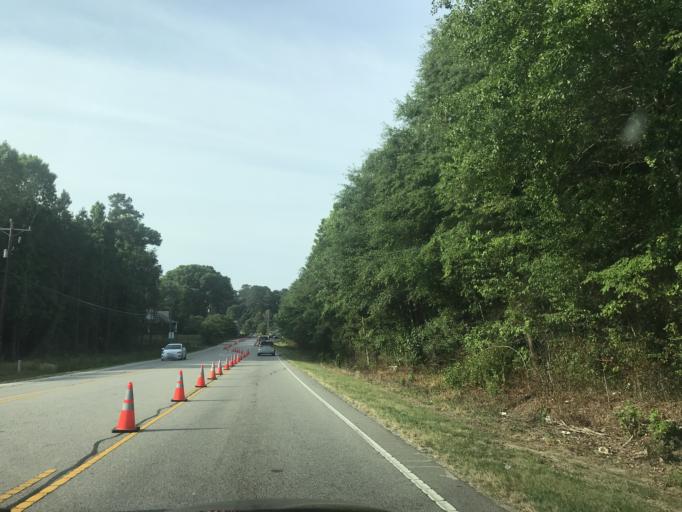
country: US
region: North Carolina
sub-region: Wake County
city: Garner
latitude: 35.7489
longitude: -78.5861
